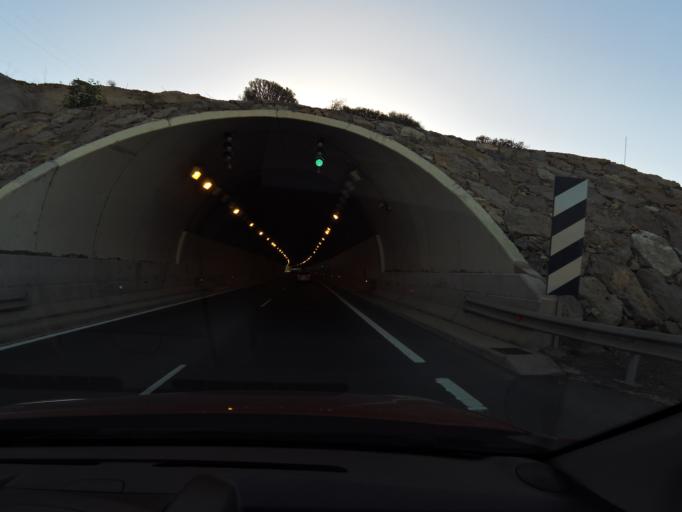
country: ES
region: Canary Islands
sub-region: Provincia de Las Palmas
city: Puerto Rico
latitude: 27.7874
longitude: -15.6913
